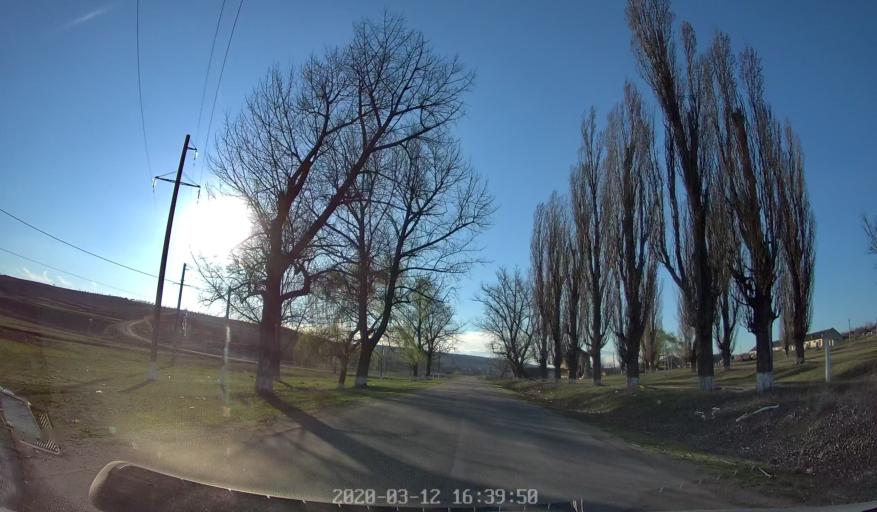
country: MD
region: Anenii Noi
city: Anenii Noi
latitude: 46.8160
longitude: 29.1581
